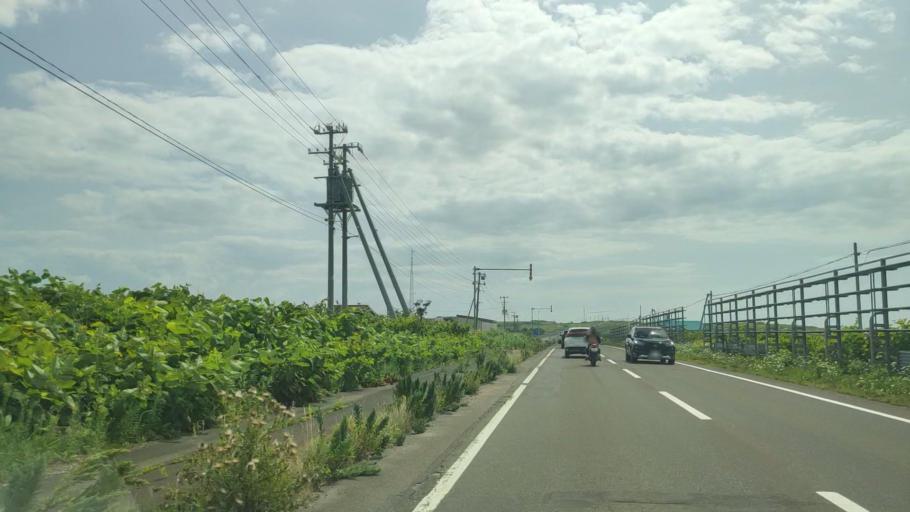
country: JP
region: Hokkaido
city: Rumoi
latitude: 44.4514
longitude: 141.7581
